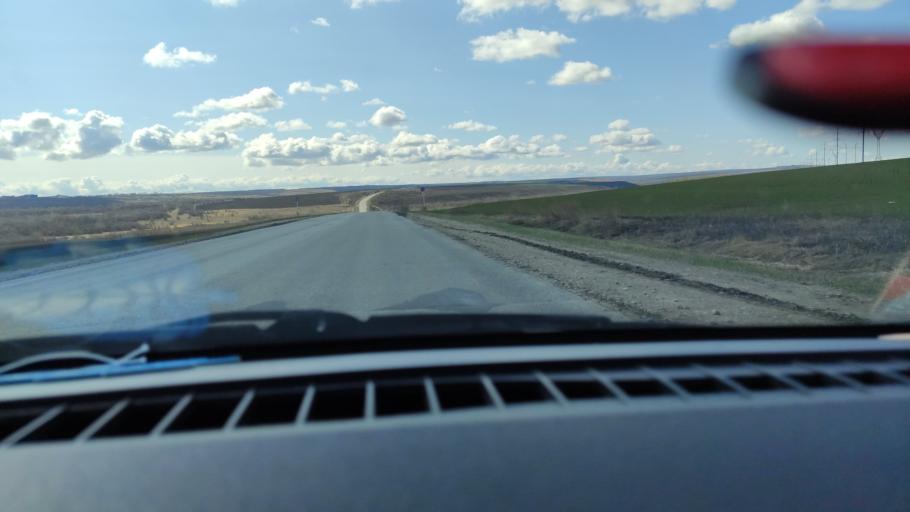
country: RU
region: Samara
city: Varlamovo
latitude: 53.0765
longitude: 48.3542
